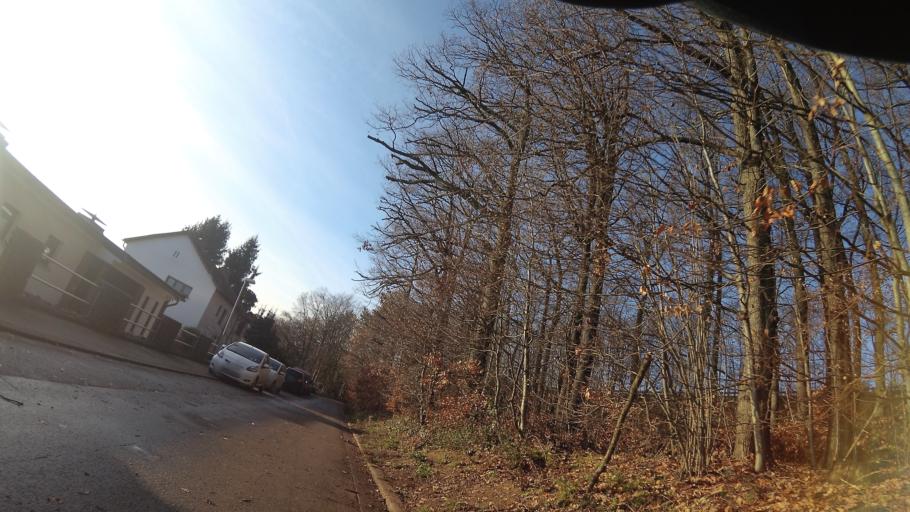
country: DE
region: Saarland
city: Spiesen-Elversberg
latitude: 49.3239
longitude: 7.1596
